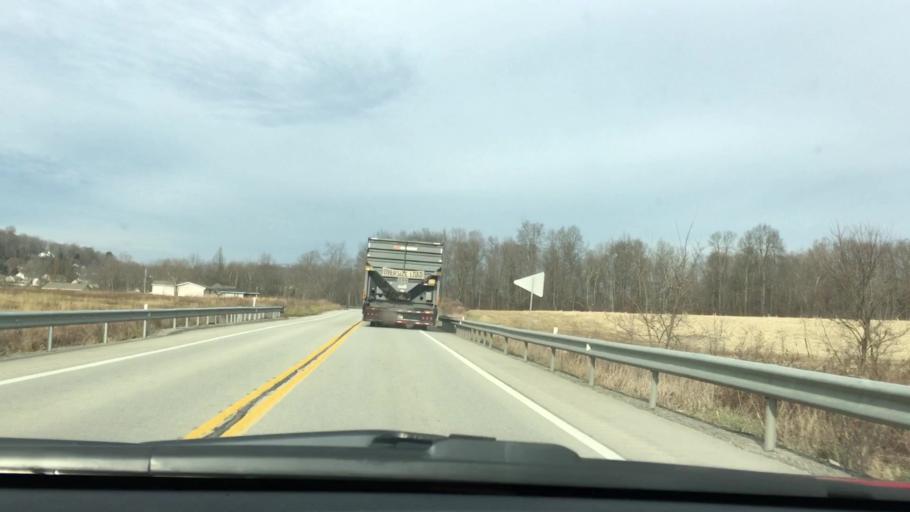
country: US
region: Pennsylvania
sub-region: Greene County
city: Fairdale
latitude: 39.8687
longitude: -79.9740
